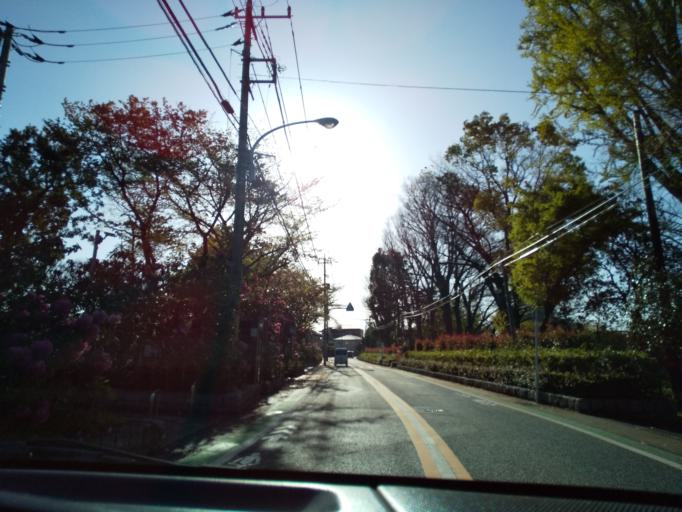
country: JP
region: Tokyo
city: Hino
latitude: 35.6979
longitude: 139.3923
